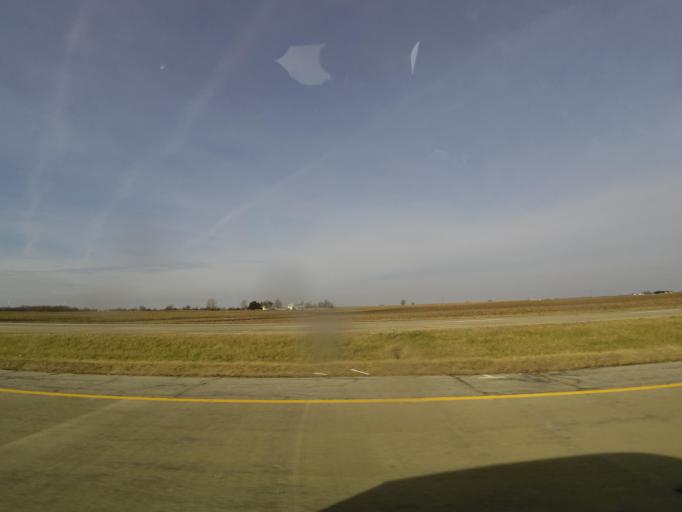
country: US
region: Illinois
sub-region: De Witt County
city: Clinton
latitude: 40.1661
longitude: -88.9784
